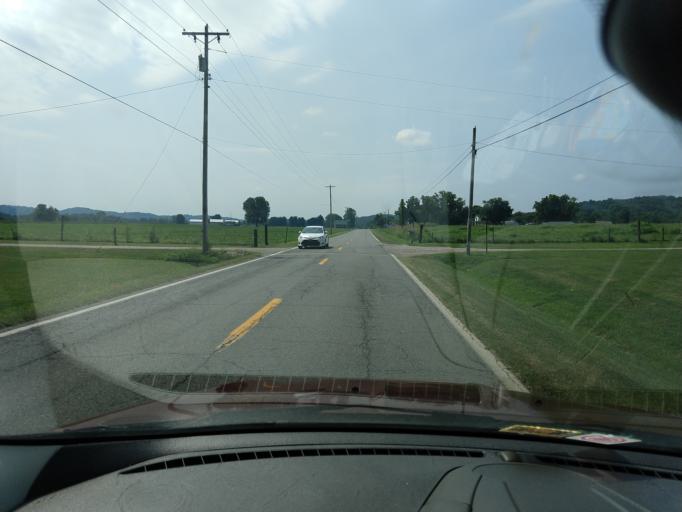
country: US
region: West Virginia
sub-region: Mason County
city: New Haven
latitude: 38.9492
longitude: -81.9210
